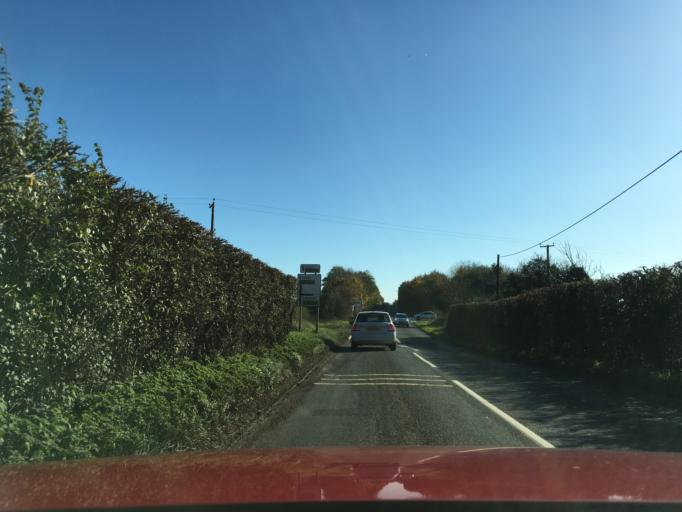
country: GB
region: England
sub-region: Somerset
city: Stoke-sub-Hamdon
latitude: 50.9768
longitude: -2.7321
